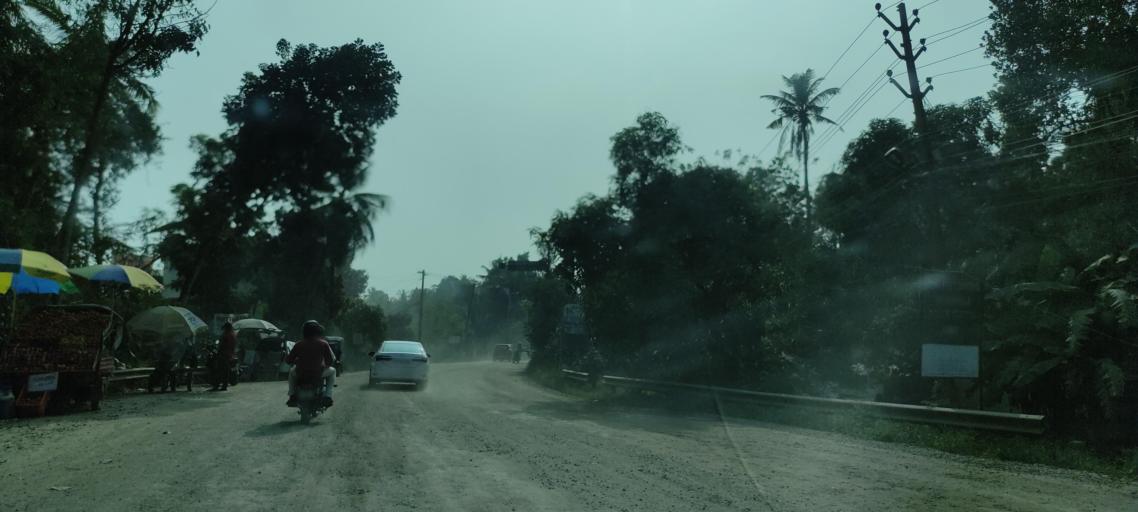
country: IN
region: Kerala
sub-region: Pattanamtitta
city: Tiruvalla
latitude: 9.3740
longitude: 76.5536
